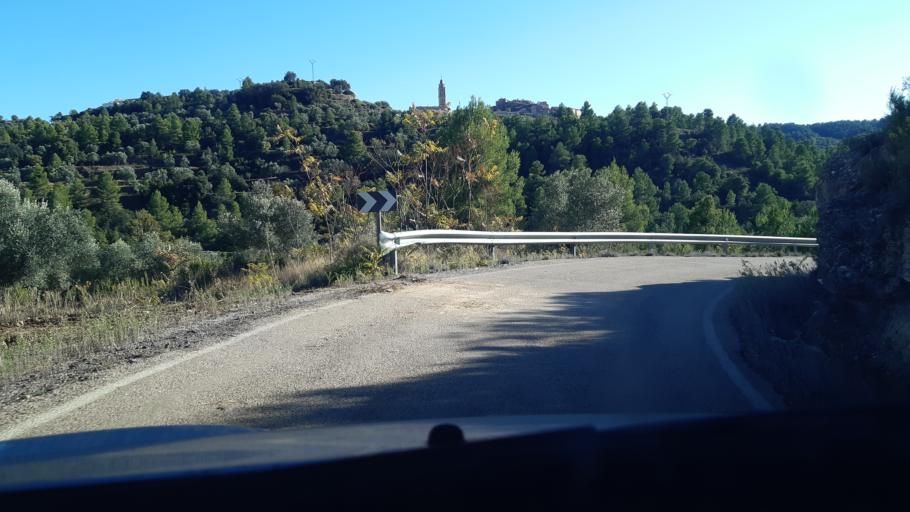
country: ES
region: Aragon
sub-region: Provincia de Teruel
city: Fornoles
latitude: 40.9007
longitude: -0.0052
